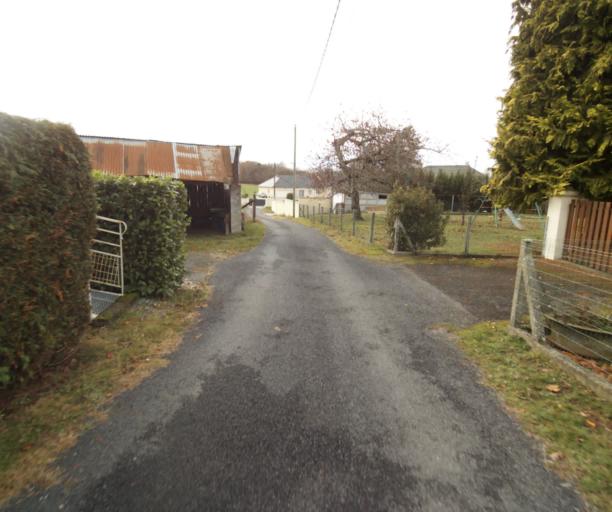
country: FR
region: Limousin
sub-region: Departement de la Correze
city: Saint-Mexant
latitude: 45.2689
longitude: 1.6791
